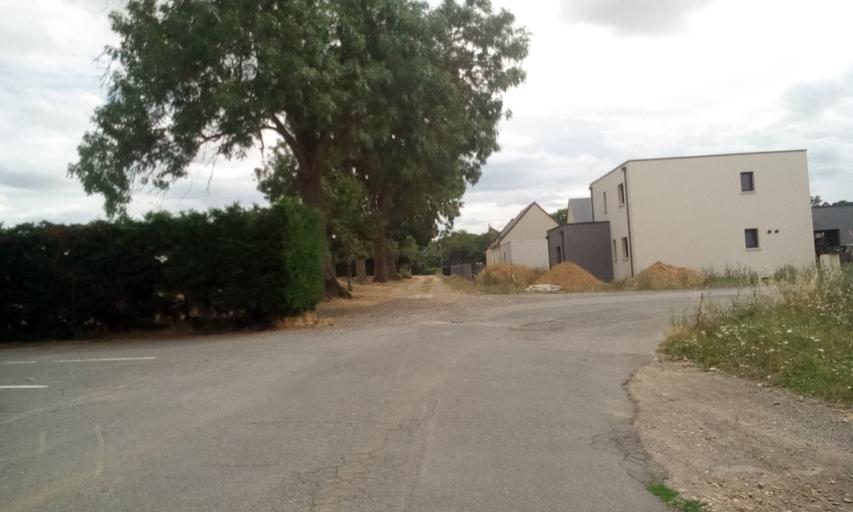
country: FR
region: Lower Normandy
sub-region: Departement du Calvados
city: Bellengreville
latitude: 49.1188
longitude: -0.2005
